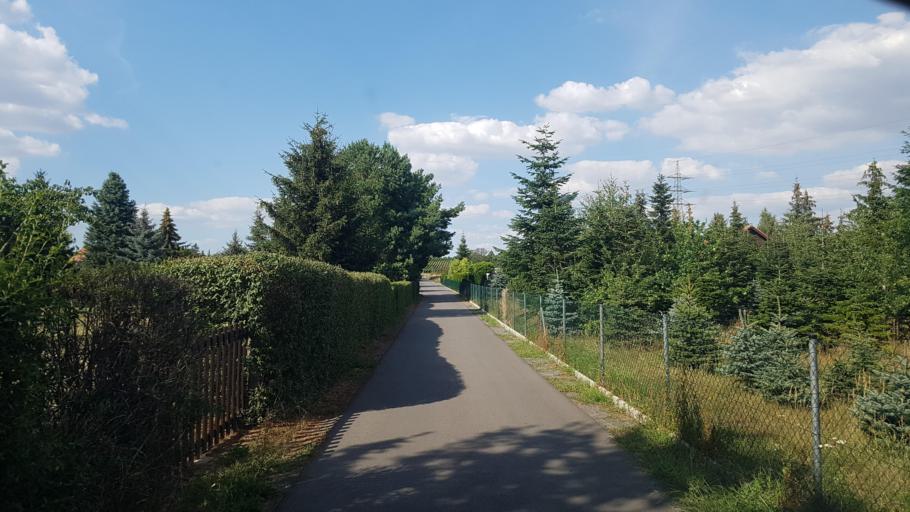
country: DE
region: Saxony-Anhalt
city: Jessen
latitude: 51.7947
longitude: 12.9746
